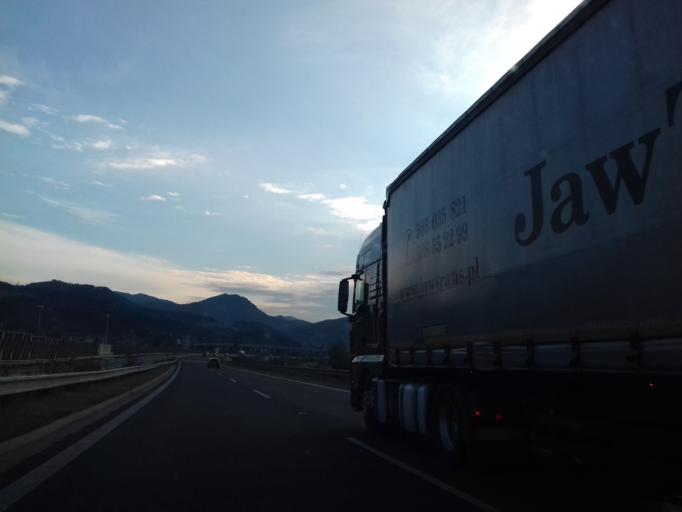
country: SK
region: Zilinsky
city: Bytca
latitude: 49.2410
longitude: 18.6419
